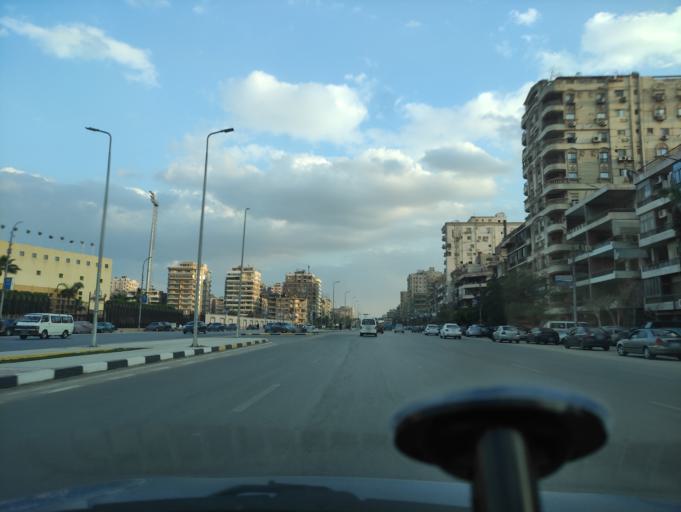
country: EG
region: Muhafazat al Qalyubiyah
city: Al Khankah
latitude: 30.1169
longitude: 31.3417
